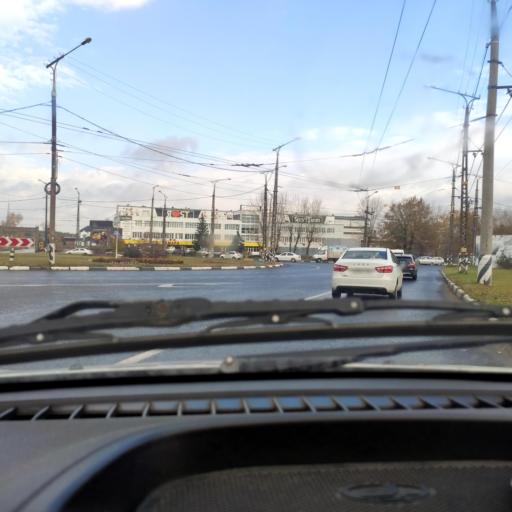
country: RU
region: Samara
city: Zhigulevsk
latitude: 53.4860
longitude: 49.4865
